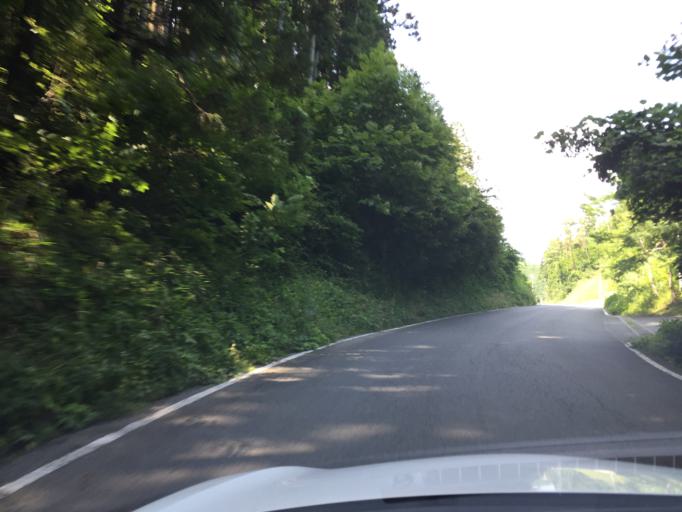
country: JP
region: Fukushima
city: Iwaki
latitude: 36.9832
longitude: 140.7003
